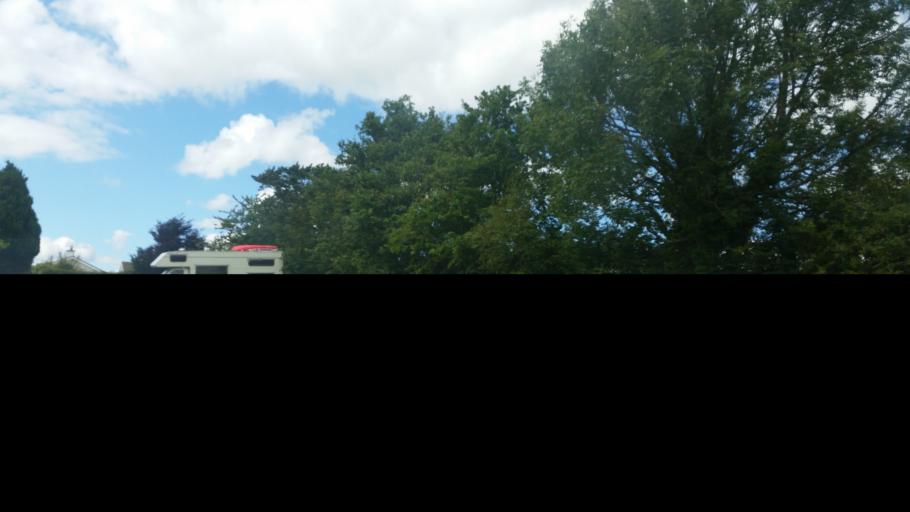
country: IE
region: Munster
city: Carrick-on-Suir
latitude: 52.2890
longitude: -7.4602
